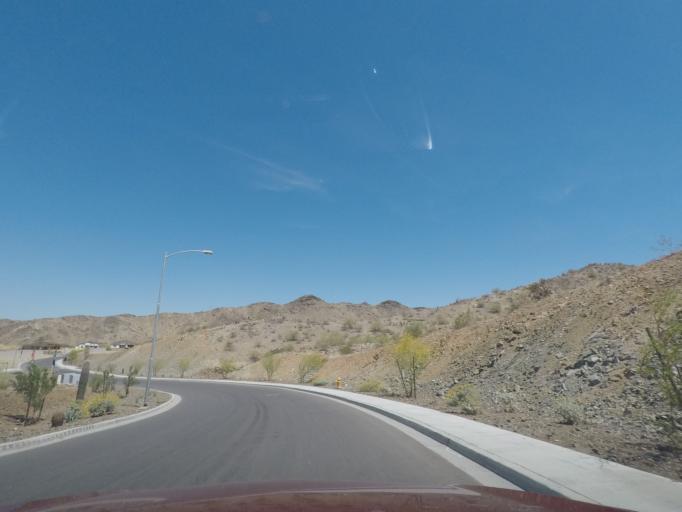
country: US
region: Arizona
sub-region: Maricopa County
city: Laveen
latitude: 33.2977
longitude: -112.1352
